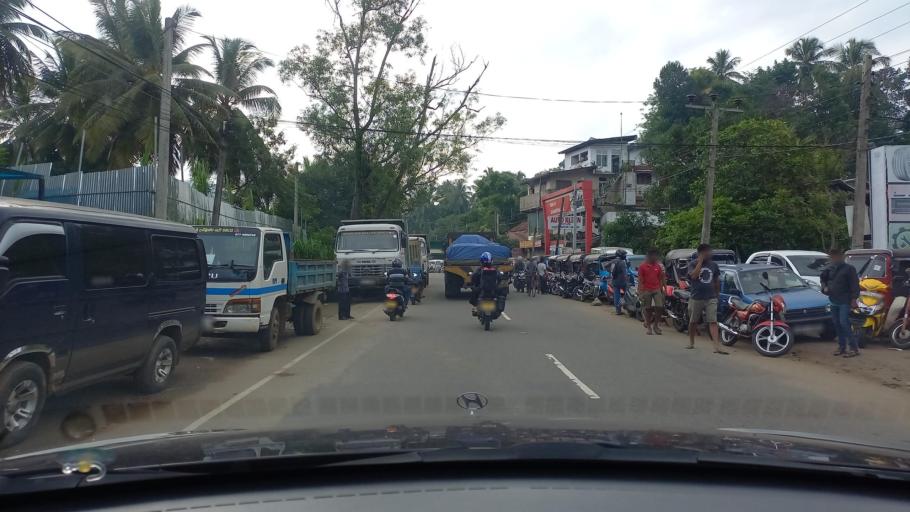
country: LK
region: Central
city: Kadugannawa
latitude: 7.2492
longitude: 80.4586
